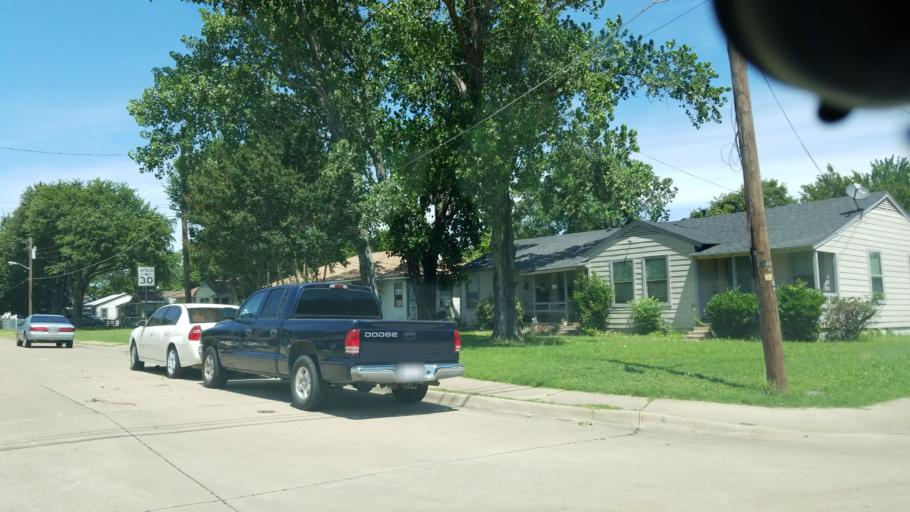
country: US
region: Texas
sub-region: Dallas County
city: Irving
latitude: 32.8196
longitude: -96.9300
